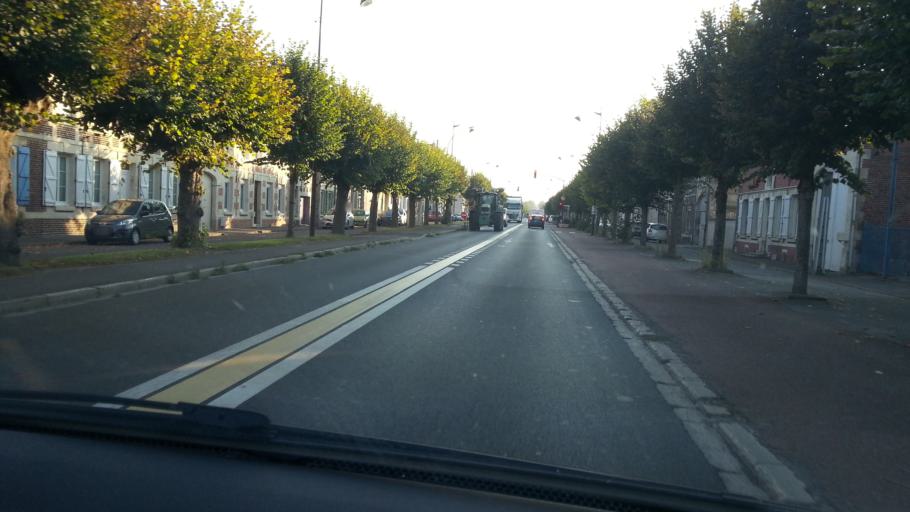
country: FR
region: Picardie
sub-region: Departement de l'Oise
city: Estrees-Saint-Denis
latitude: 49.4285
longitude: 2.6391
